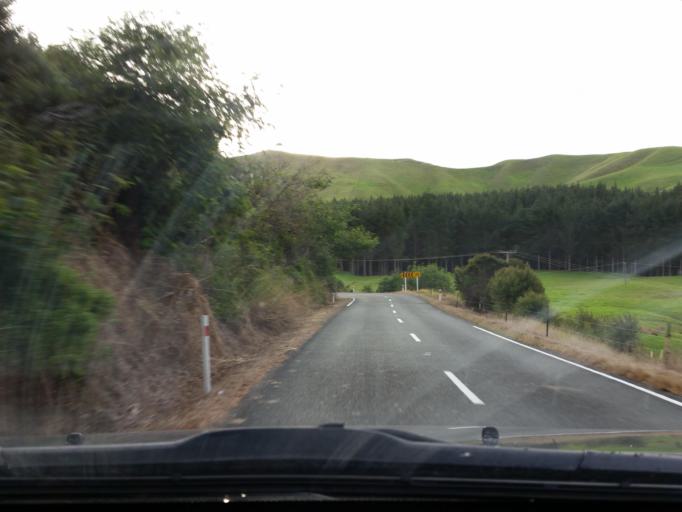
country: NZ
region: Northland
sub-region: Kaipara District
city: Dargaville
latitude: -35.8222
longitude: 173.6851
